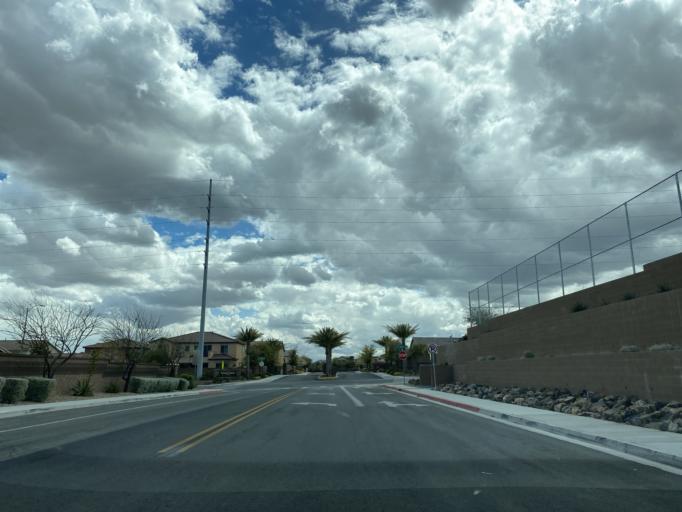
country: US
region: Nevada
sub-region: Clark County
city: Summerlin South
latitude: 36.3000
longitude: -115.3082
